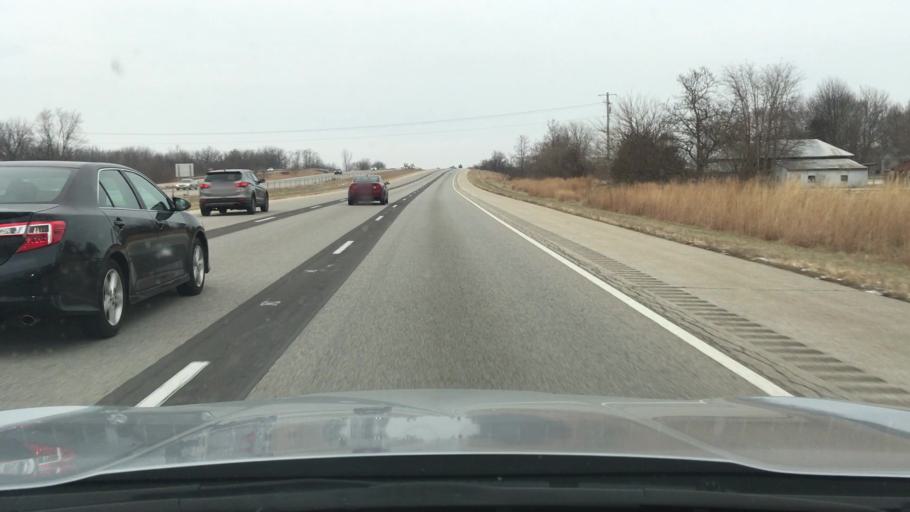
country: US
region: Illinois
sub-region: Sangamon County
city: Divernon
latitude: 39.6238
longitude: -89.6468
